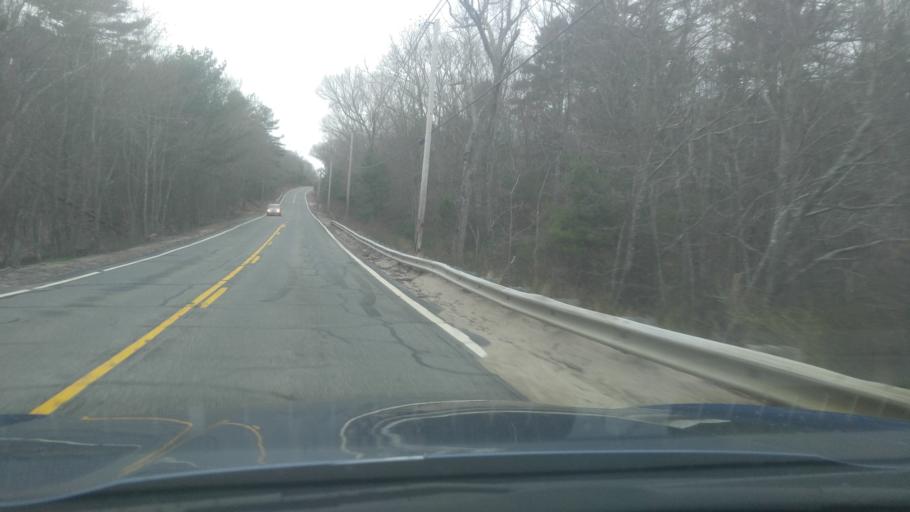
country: US
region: Rhode Island
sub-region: Kent County
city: West Greenwich
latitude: 41.6739
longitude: -71.6401
